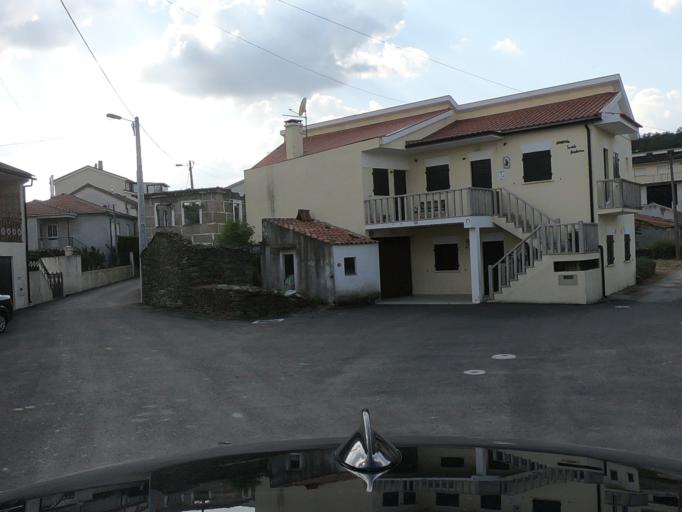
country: PT
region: Vila Real
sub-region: Sabrosa
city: Vilela
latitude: 41.2408
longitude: -7.6517
